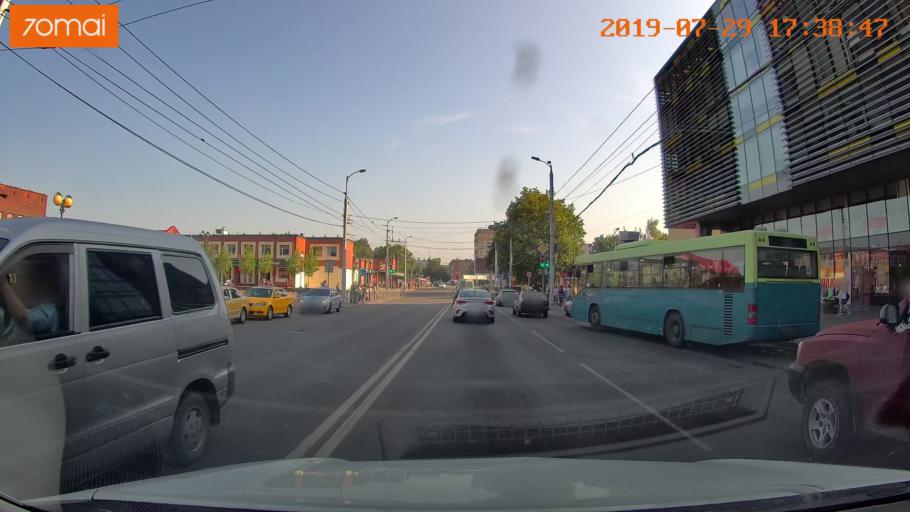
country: RU
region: Kaliningrad
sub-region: Gorod Kaliningrad
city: Kaliningrad
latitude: 54.7213
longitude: 20.5073
